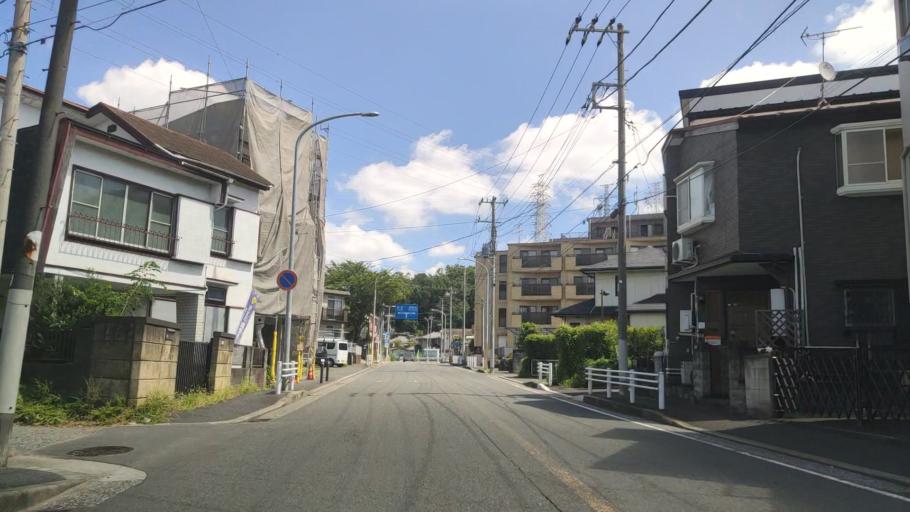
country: JP
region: Kanagawa
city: Yokohama
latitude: 35.5294
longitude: 139.6201
